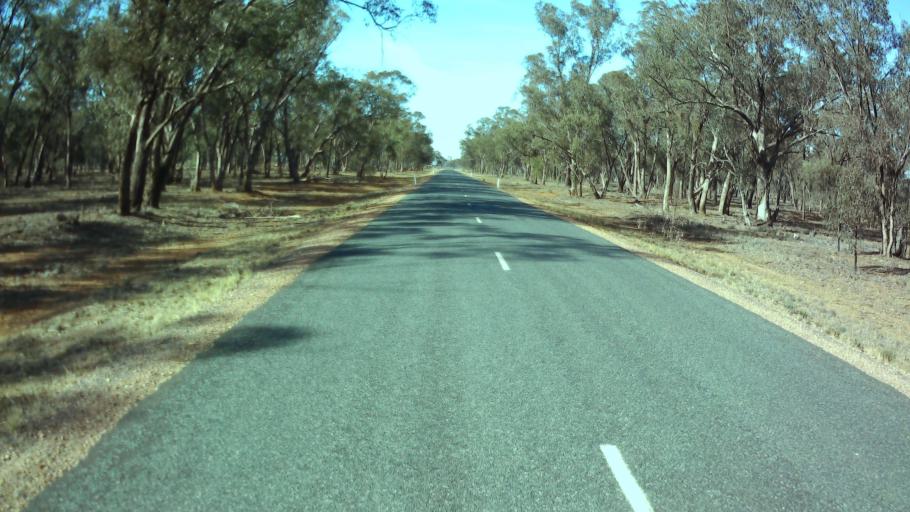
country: AU
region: New South Wales
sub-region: Weddin
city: Grenfell
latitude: -34.0632
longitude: 147.9085
